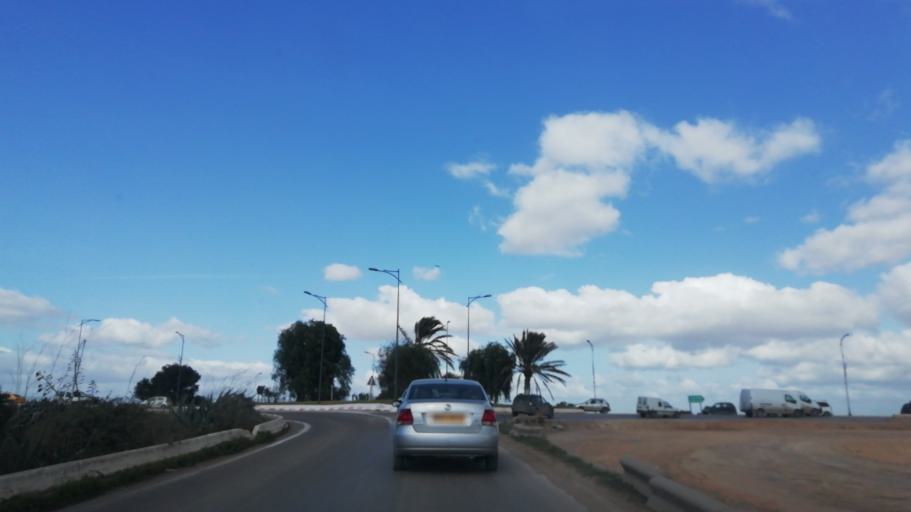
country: DZ
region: Oran
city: Es Senia
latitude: 35.6238
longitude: -0.5877
